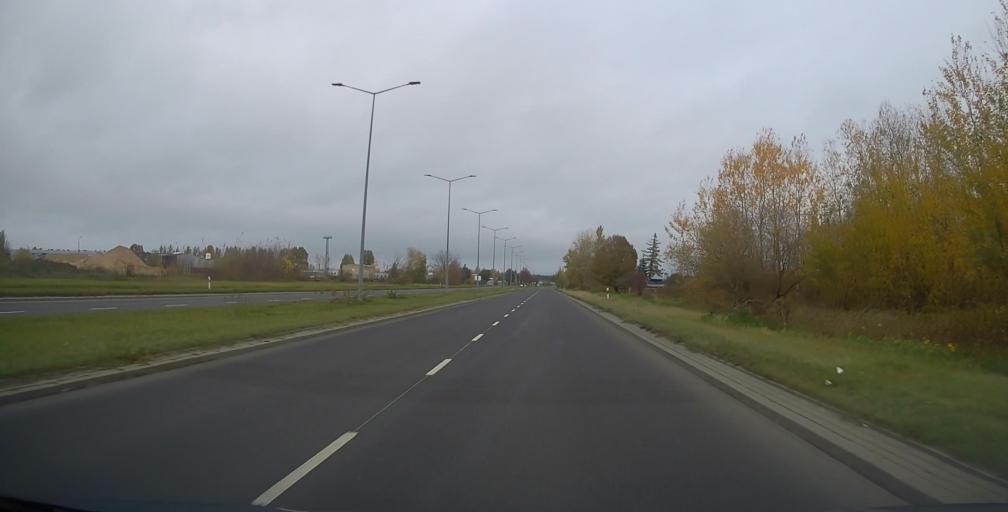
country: PL
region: Warmian-Masurian Voivodeship
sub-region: Powiat elcki
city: Elk
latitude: 53.8220
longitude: 22.3899
